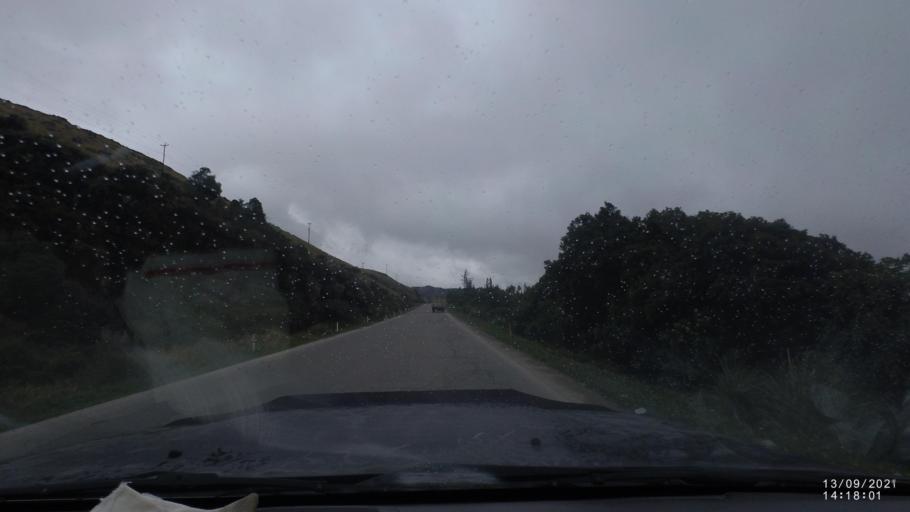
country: BO
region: Cochabamba
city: Colomi
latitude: -17.2292
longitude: -65.8876
